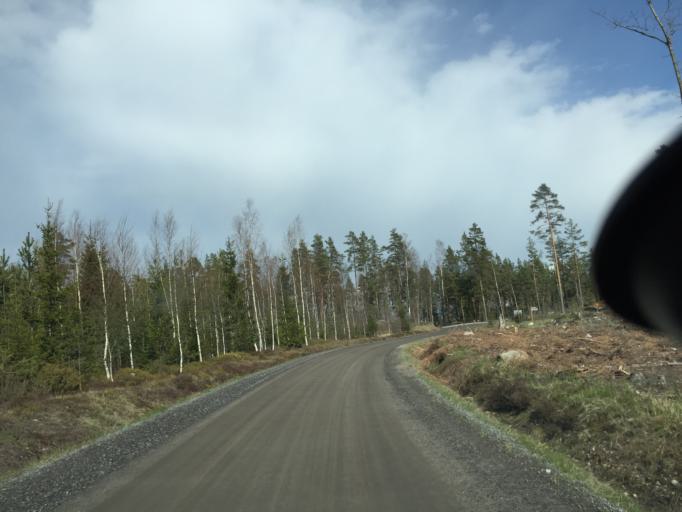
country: FI
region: Uusimaa
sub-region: Raaseporin
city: Hanko
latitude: 59.9426
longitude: 22.9498
